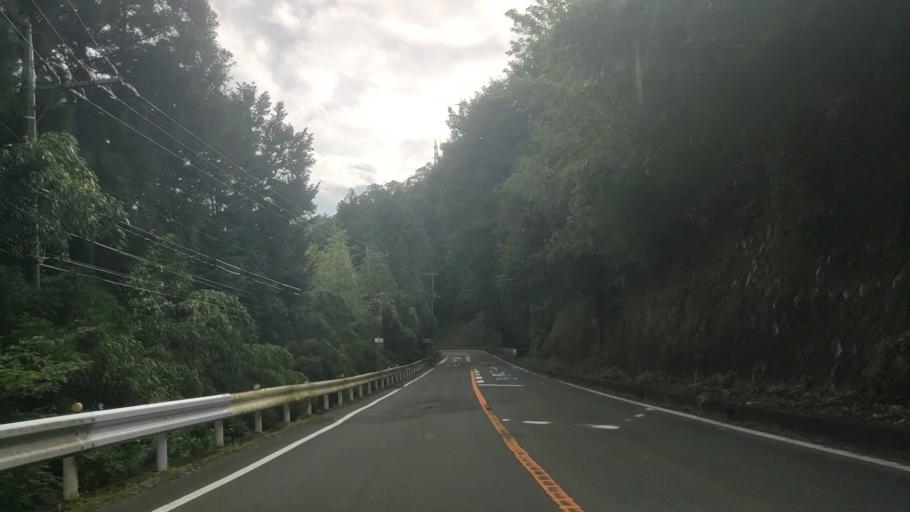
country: JP
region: Gunma
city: Omamacho-omama
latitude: 36.5781
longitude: 139.3891
